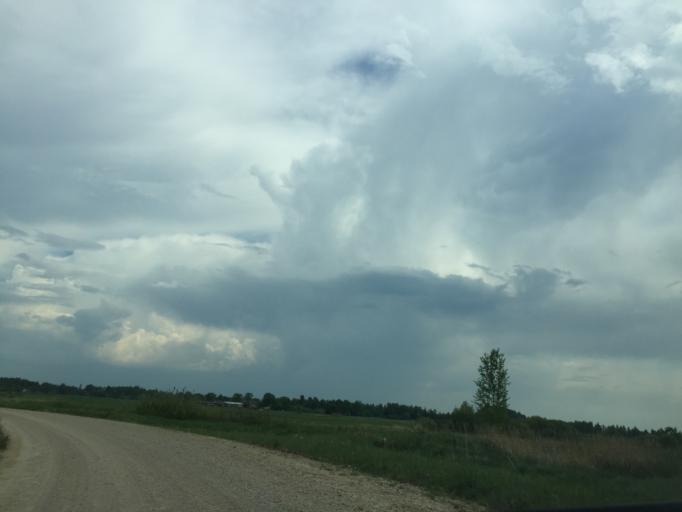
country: LV
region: Livani
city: Livani
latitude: 56.5496
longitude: 26.2301
